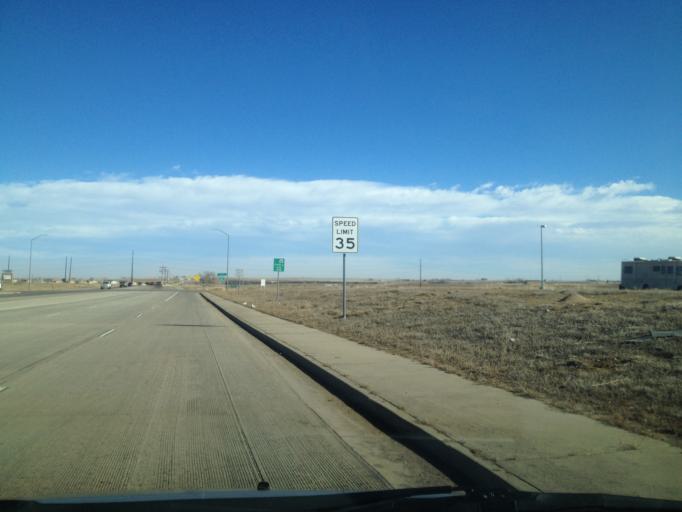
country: US
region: Colorado
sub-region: Weld County
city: Dacono
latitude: 40.0438
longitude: -104.9783
